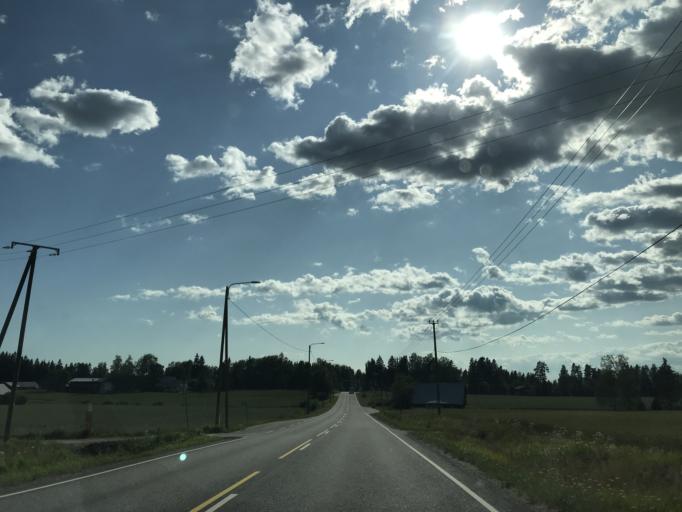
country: FI
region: Uusimaa
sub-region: Helsinki
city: Nurmijaervi
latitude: 60.4619
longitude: 24.7446
